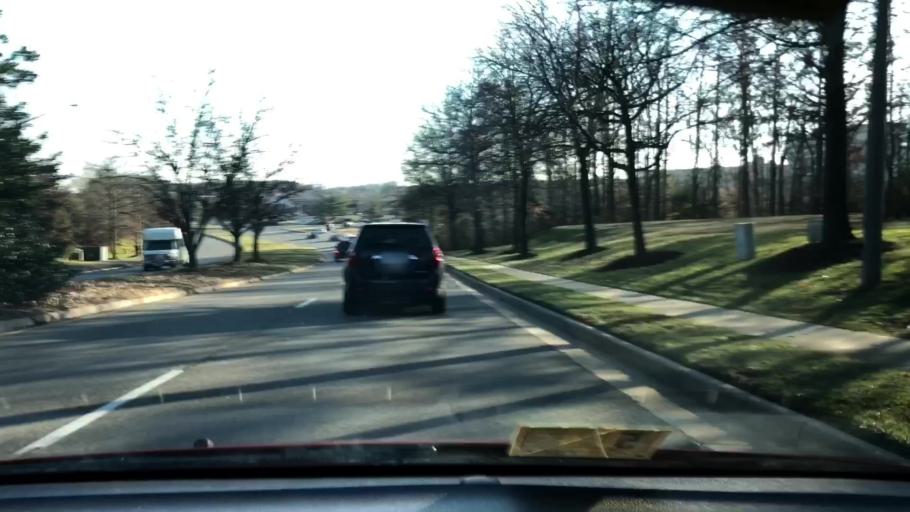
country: US
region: Virginia
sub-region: Fairfax County
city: Franconia
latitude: 38.7773
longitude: -77.1355
